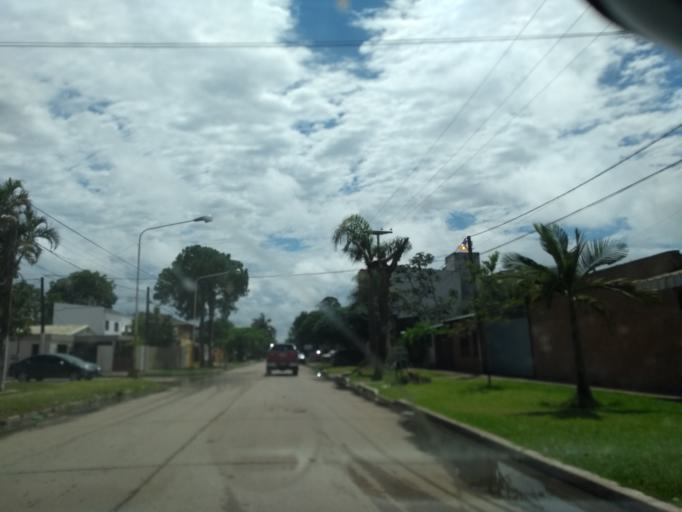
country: AR
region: Chaco
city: Barranqueras
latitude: -27.4821
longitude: -58.9497
